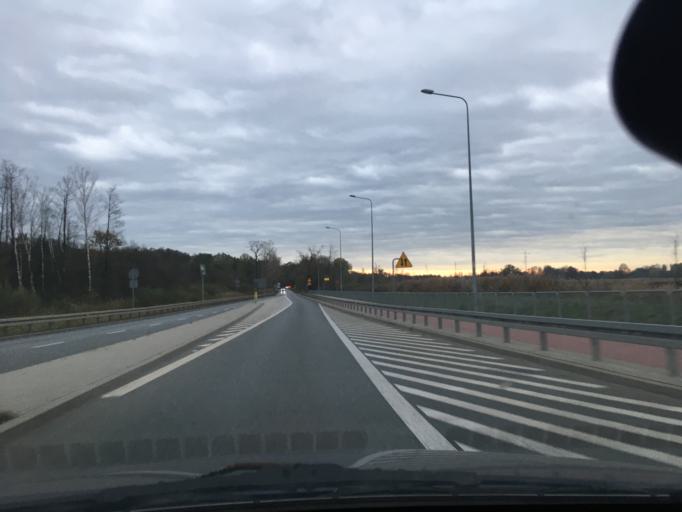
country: PL
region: Masovian Voivodeship
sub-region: Powiat pruszkowski
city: Nadarzyn
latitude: 52.1040
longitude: 20.8392
